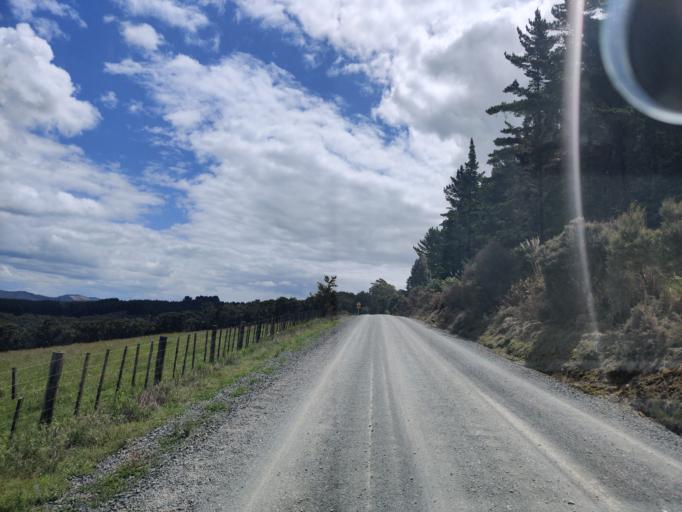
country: NZ
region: Northland
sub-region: Far North District
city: Paihia
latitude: -35.2593
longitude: 174.0639
